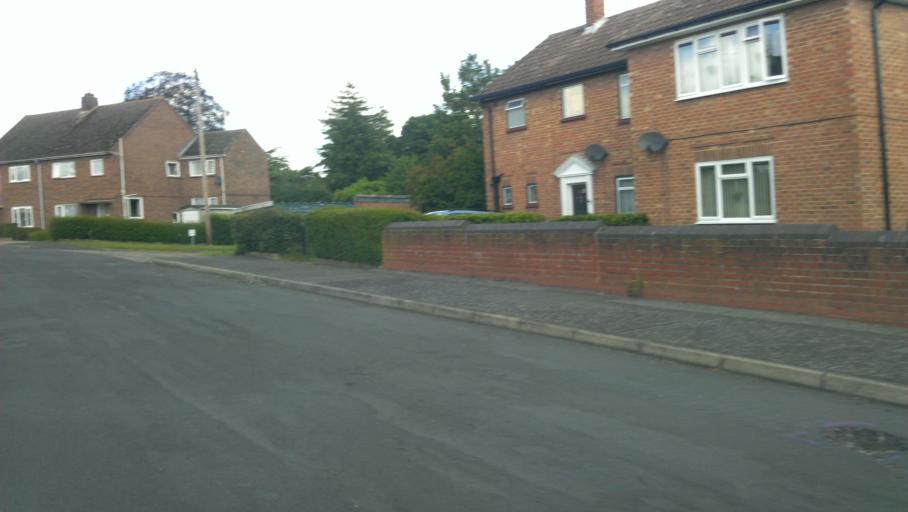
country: GB
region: England
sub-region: Essex
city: Colchester
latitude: 51.8751
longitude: 0.9103
